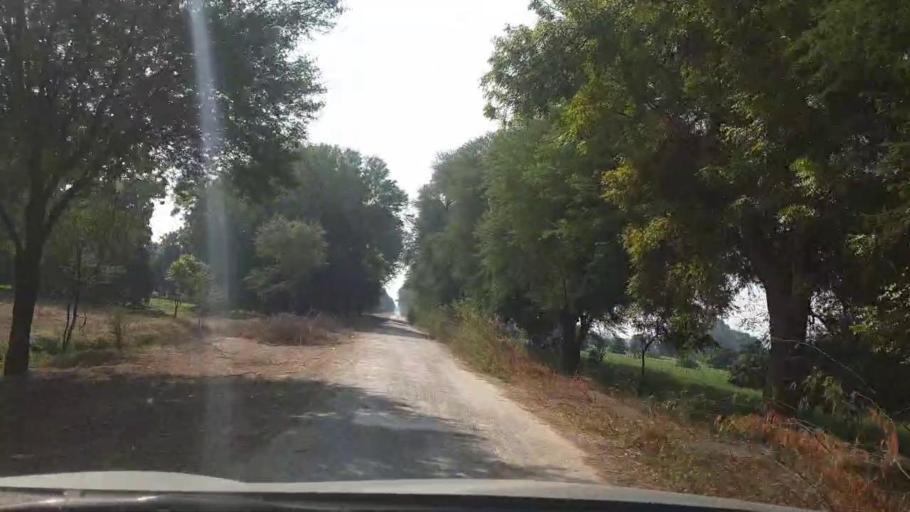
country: PK
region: Sindh
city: Tando Allahyar
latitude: 25.5178
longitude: 68.7861
